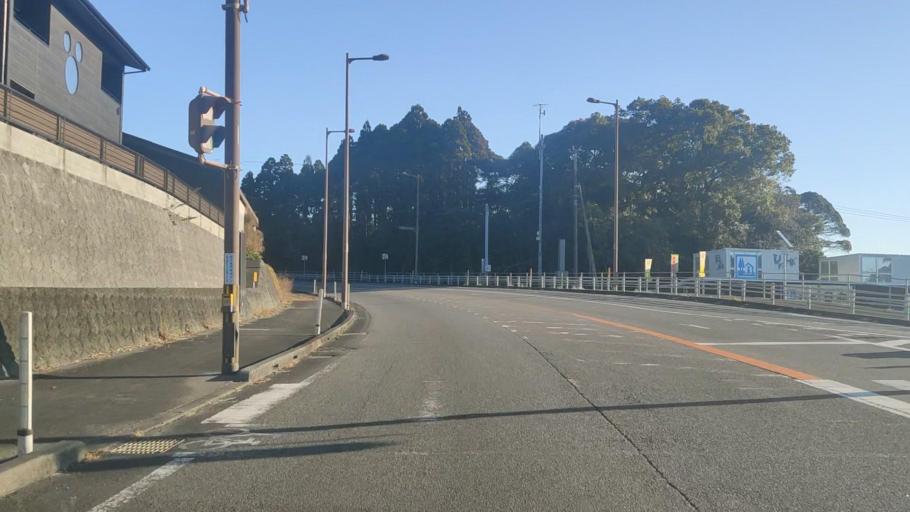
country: JP
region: Miyazaki
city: Takanabe
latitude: 32.3433
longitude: 131.6234
